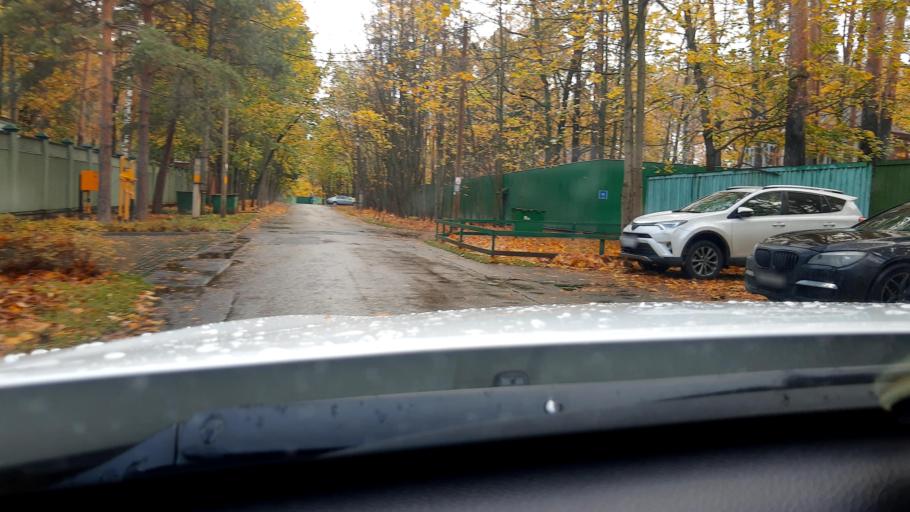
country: RU
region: Moscow
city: Shchukino
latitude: 55.7862
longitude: 37.4417
